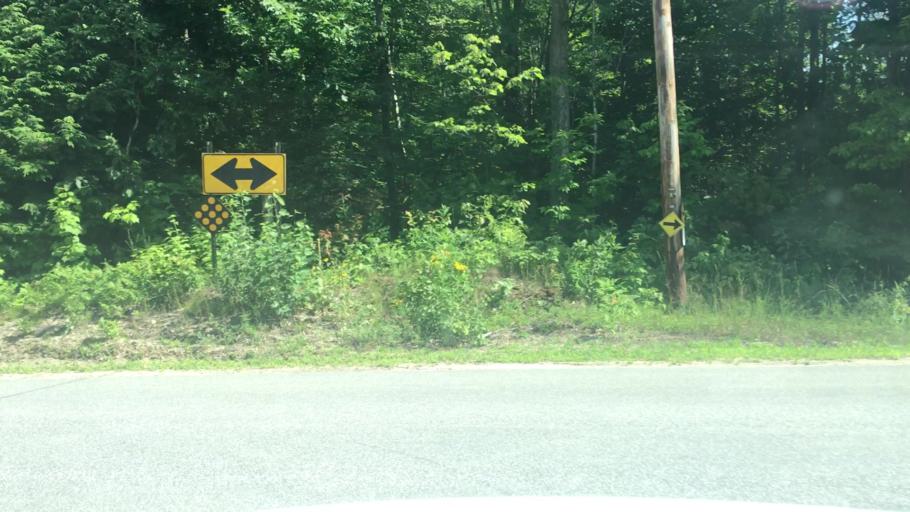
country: US
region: Maine
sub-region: Oxford County
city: West Paris
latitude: 44.3258
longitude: -70.5086
